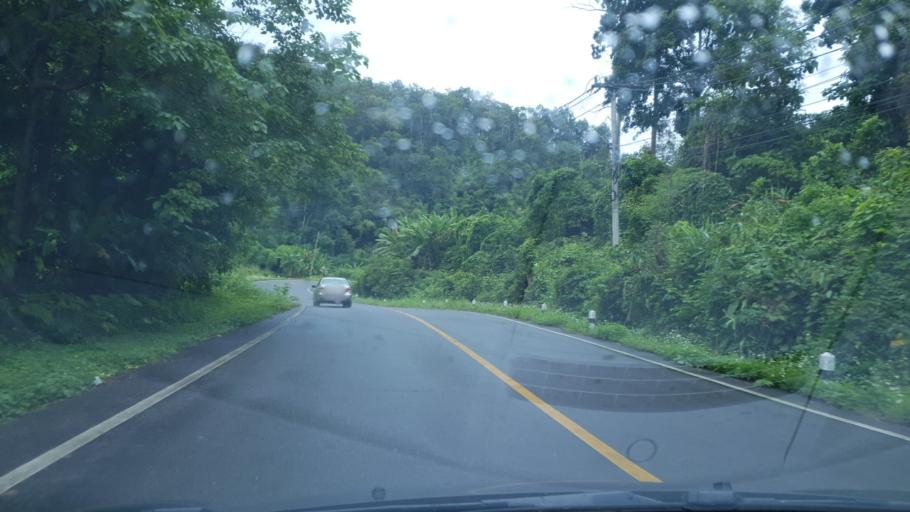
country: TH
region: Mae Hong Son
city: Mae La Noi
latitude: 18.5706
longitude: 97.9331
